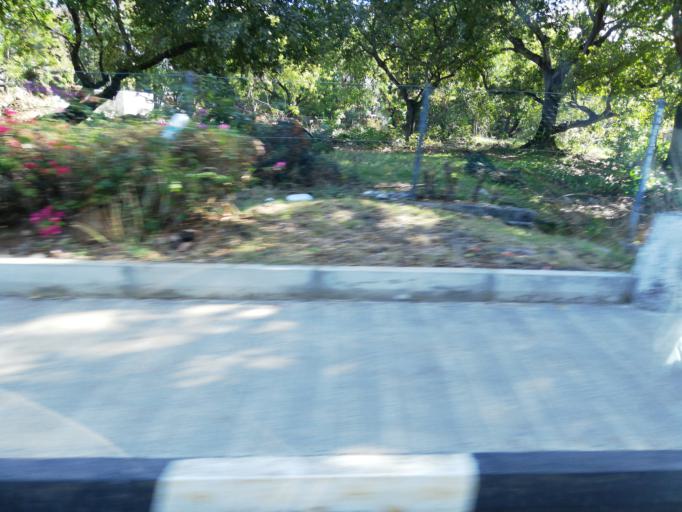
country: MU
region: Port Louis
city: Port Louis
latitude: -20.1605
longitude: 57.4902
